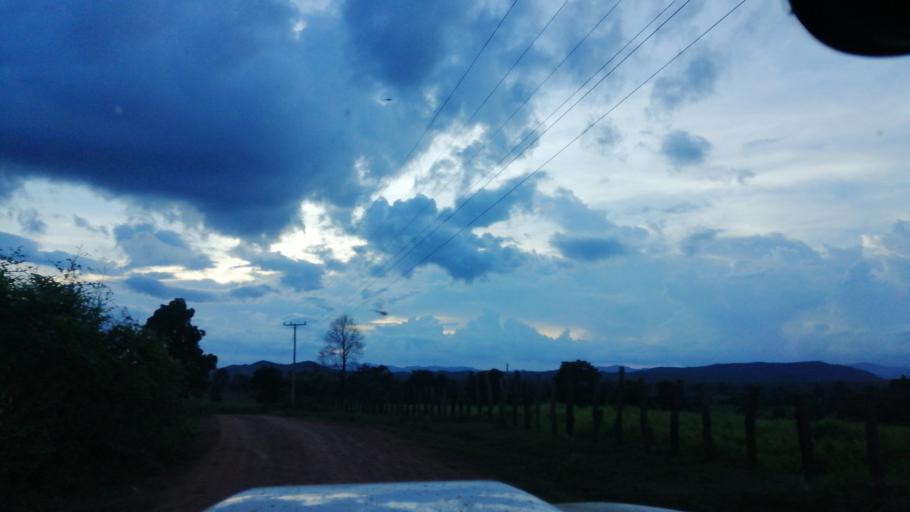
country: TH
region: Uttaradit
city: Ban Khok
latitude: 17.8786
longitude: 101.0623
